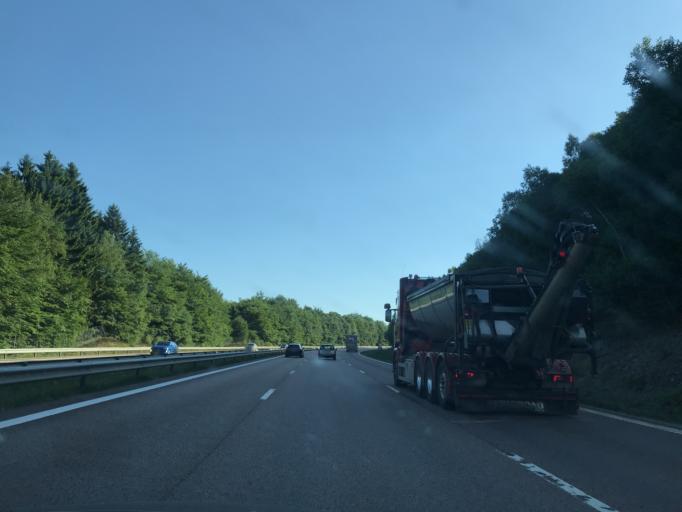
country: SE
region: Skane
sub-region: Bastads Kommun
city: Forslov
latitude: 56.3458
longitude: 12.9198
